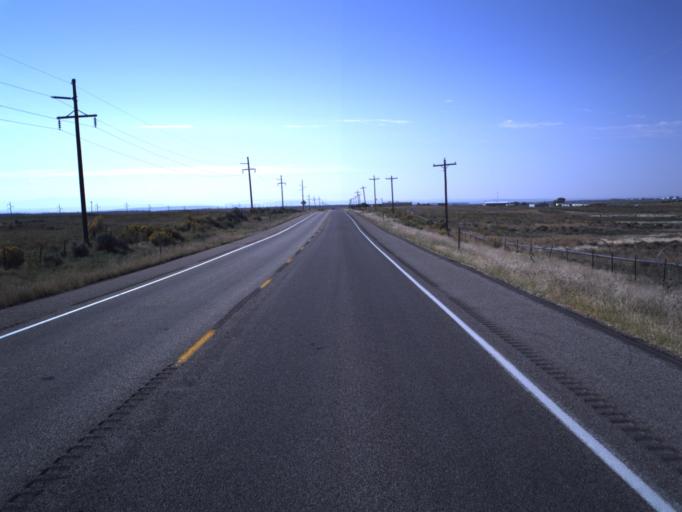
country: US
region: Utah
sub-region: San Juan County
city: Blanding
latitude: 37.5928
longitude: -109.4785
